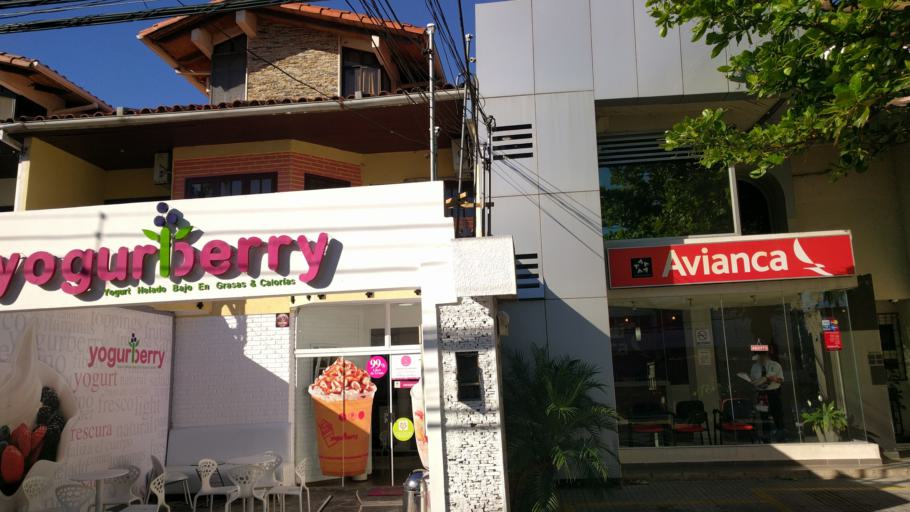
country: BO
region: Santa Cruz
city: Santa Cruz de la Sierra
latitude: -17.7615
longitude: -63.1978
